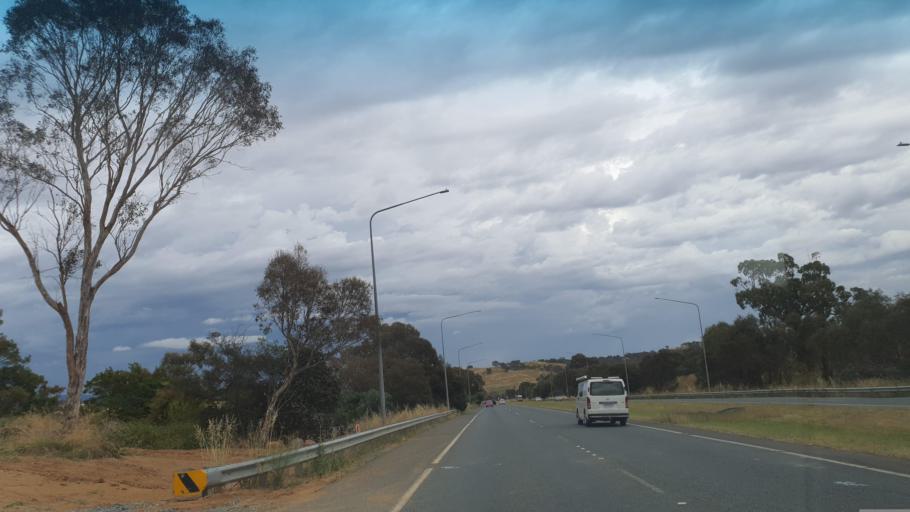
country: AU
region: Australian Capital Territory
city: Macquarie
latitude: -35.2732
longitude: 149.0605
